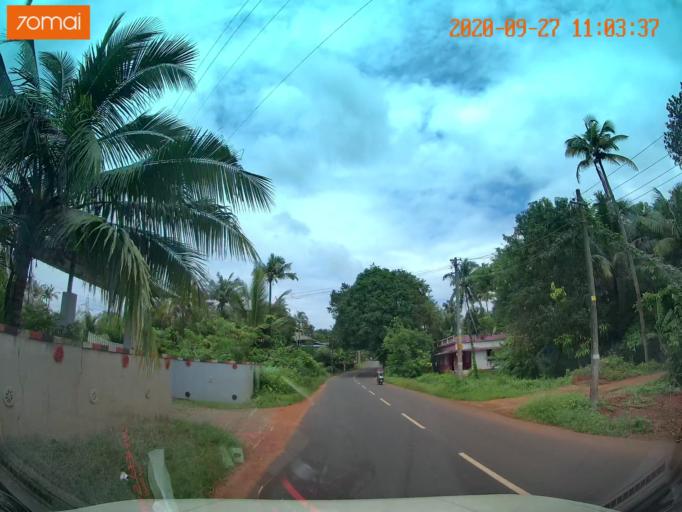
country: IN
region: Kerala
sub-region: Thrissur District
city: Irinjalakuda
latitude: 10.4219
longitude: 76.2554
